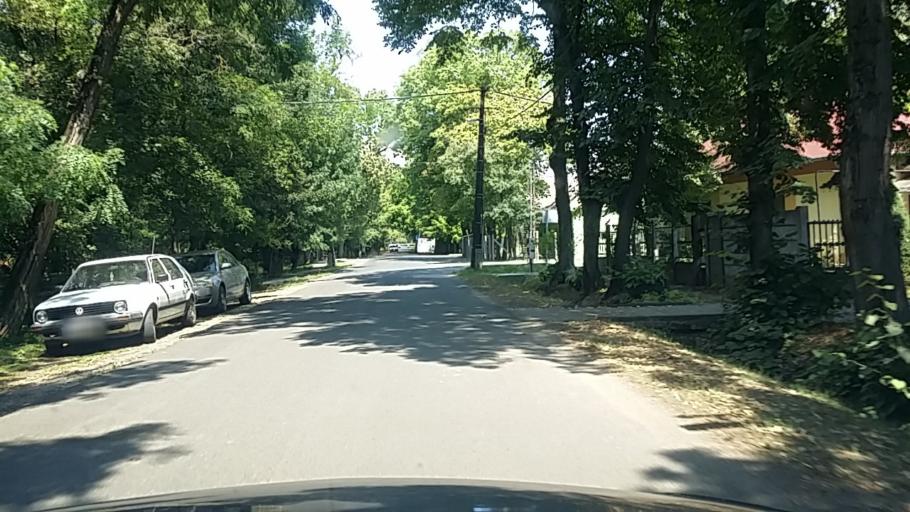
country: HU
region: Bekes
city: Gyomaendrod
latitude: 46.9381
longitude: 20.8384
